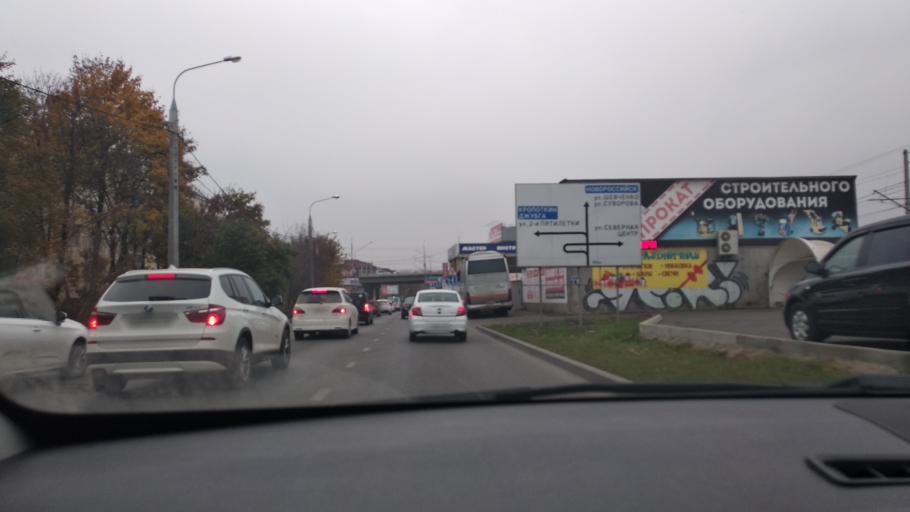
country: RU
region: Krasnodarskiy
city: Krasnodar
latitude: 45.0339
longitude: 39.0277
